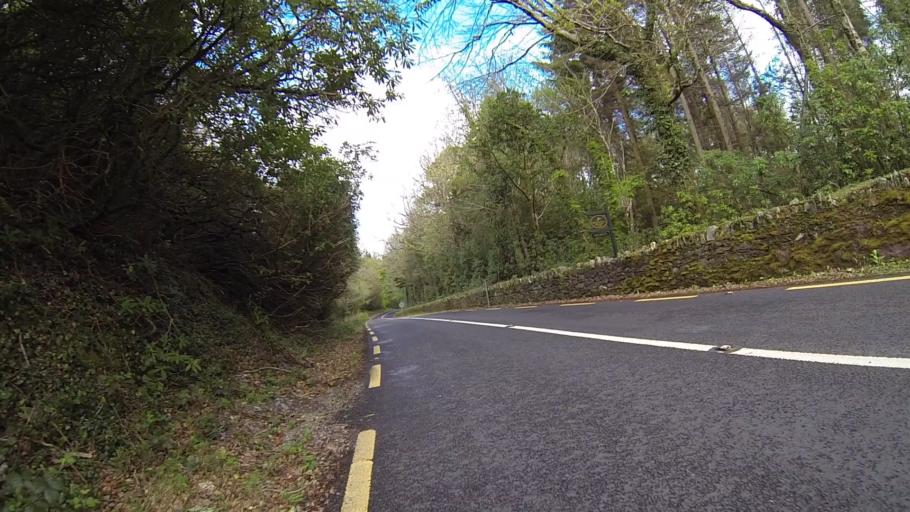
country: IE
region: Munster
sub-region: Ciarrai
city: Kenmare
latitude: 51.8182
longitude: -9.8708
